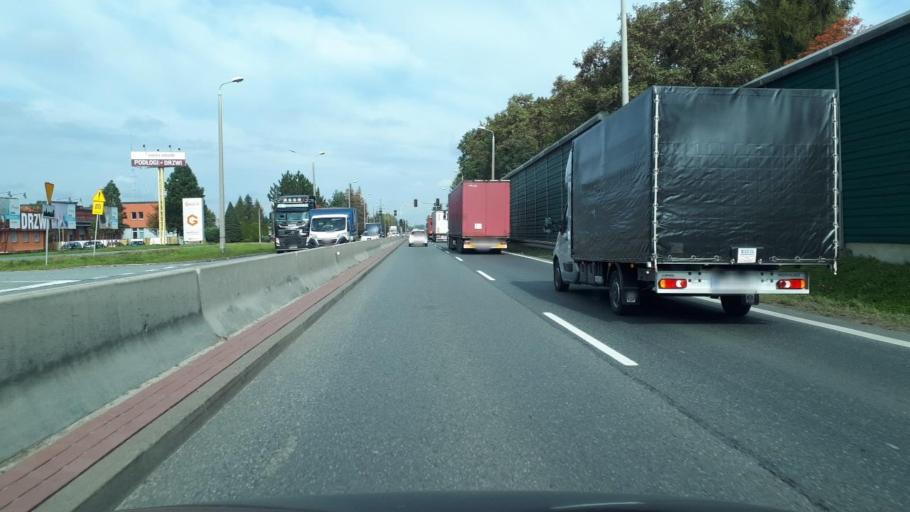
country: PL
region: Silesian Voivodeship
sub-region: Powiat pszczynski
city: Pszczyna
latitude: 49.9690
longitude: 18.9582
